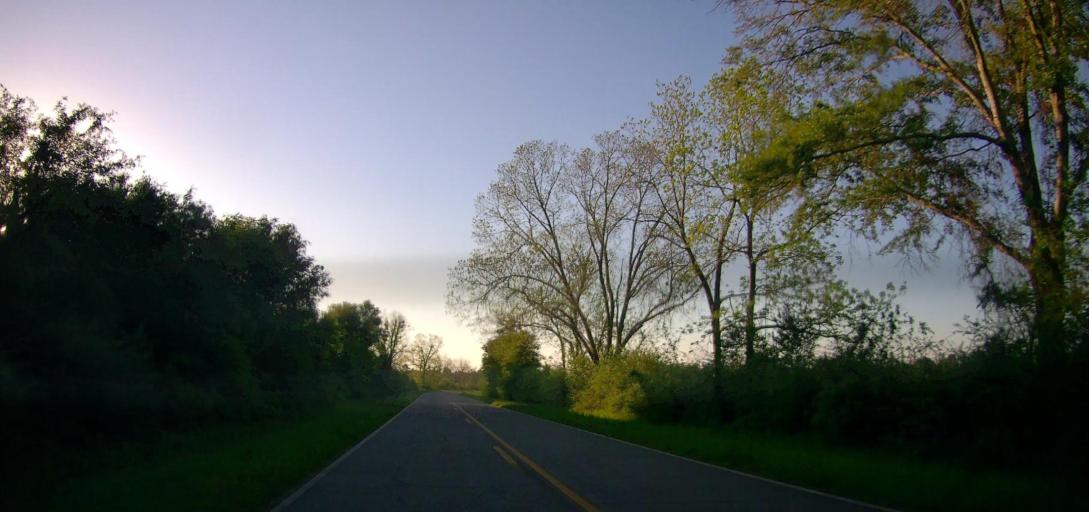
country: US
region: Georgia
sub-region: Ben Hill County
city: Fitzgerald
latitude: 31.6850
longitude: -83.2287
